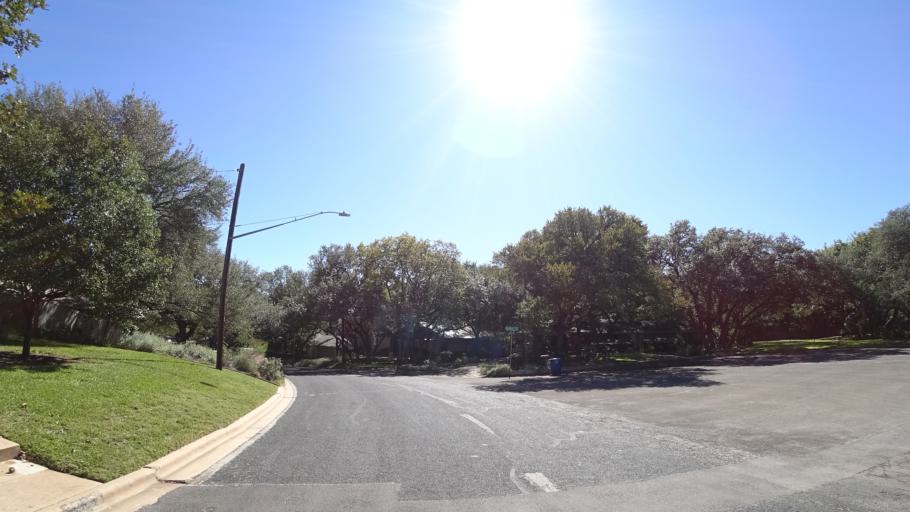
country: US
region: Texas
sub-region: Williamson County
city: Jollyville
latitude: 30.3663
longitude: -97.7643
